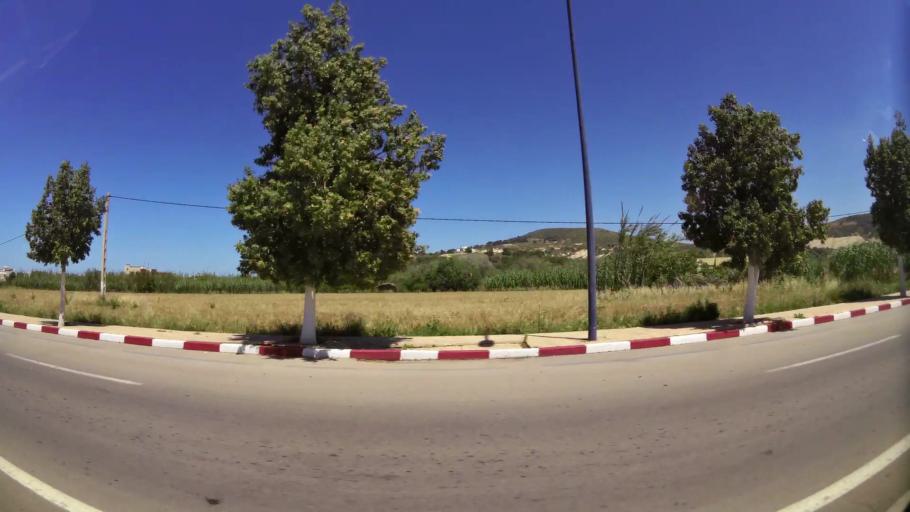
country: MA
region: Oriental
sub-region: Berkane-Taourirt
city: Madagh
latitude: 35.0692
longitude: -2.2170
